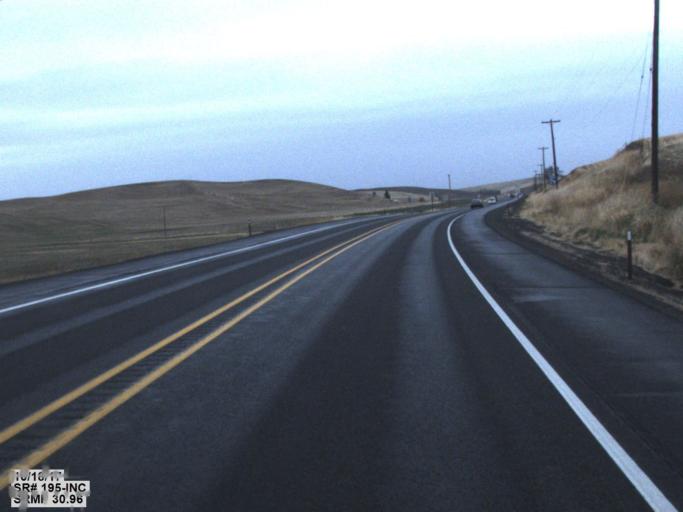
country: US
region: Washington
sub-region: Whitman County
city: Colfax
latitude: 46.7962
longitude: -117.3141
